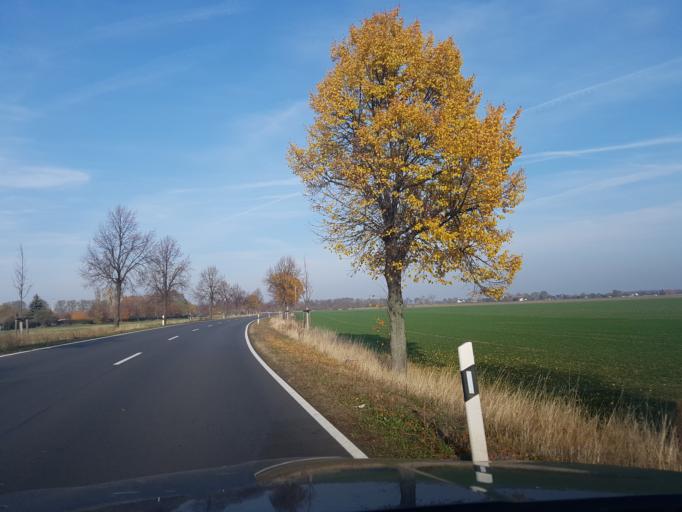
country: DE
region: Saxony
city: Torgau
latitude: 51.5581
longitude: 13.0248
